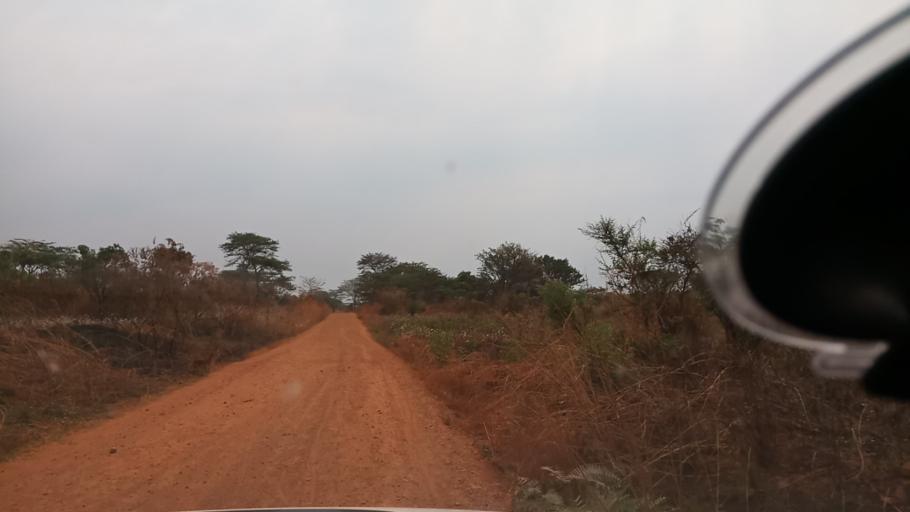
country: ZM
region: Luapula
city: Nchelenge
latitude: -9.0953
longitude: 28.3240
